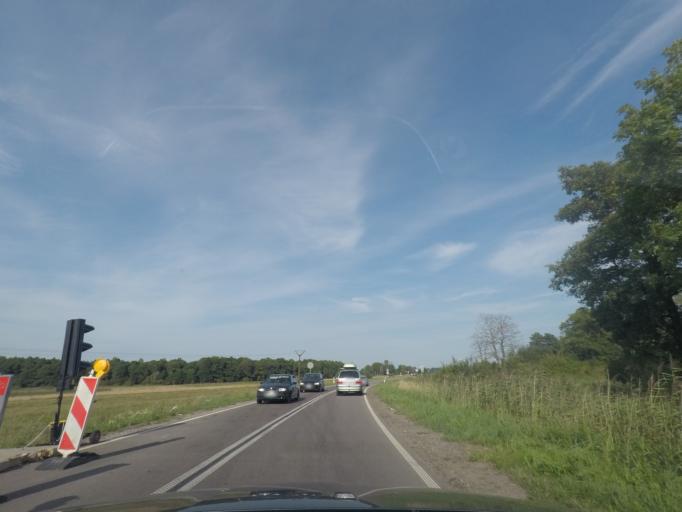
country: PL
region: Pomeranian Voivodeship
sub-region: Powiat leborski
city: Leba
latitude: 54.6546
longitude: 17.5652
